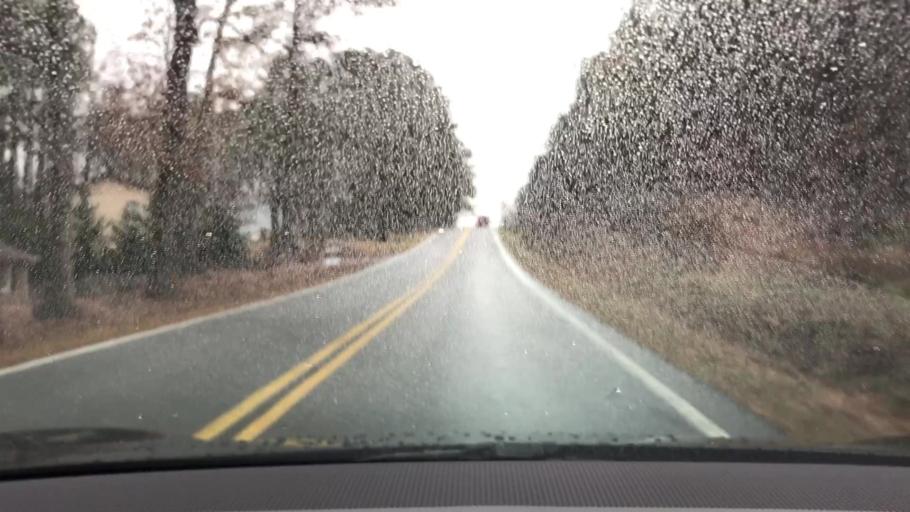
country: US
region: Georgia
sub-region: Forsyth County
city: Cumming
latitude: 34.1900
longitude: -84.1215
